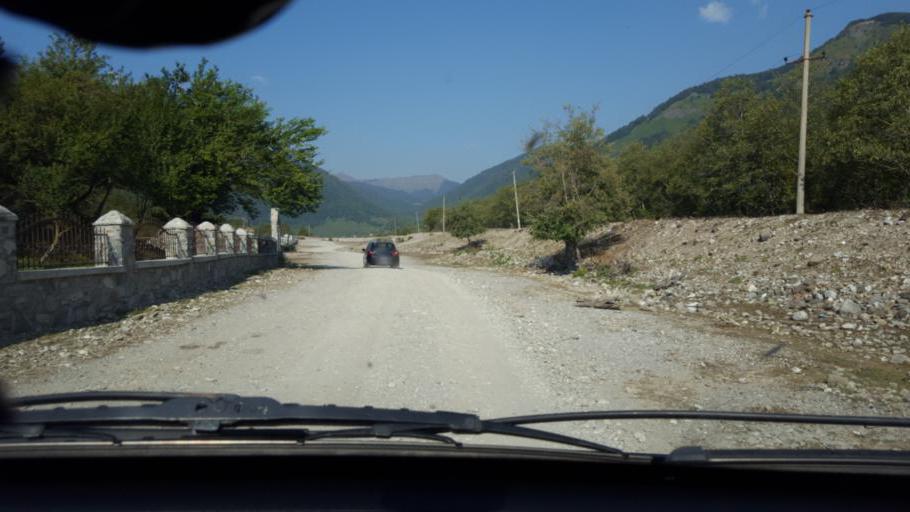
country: ME
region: Andrijevica
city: Andrijevica
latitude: 42.5931
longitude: 19.6835
